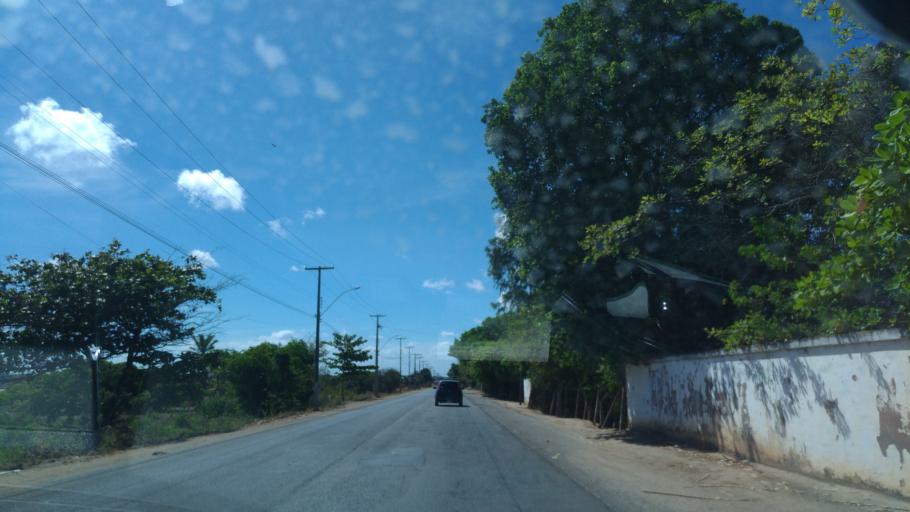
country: BR
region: Alagoas
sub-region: Marechal Deodoro
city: Marechal Deodoro
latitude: -9.7641
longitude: -35.8582
